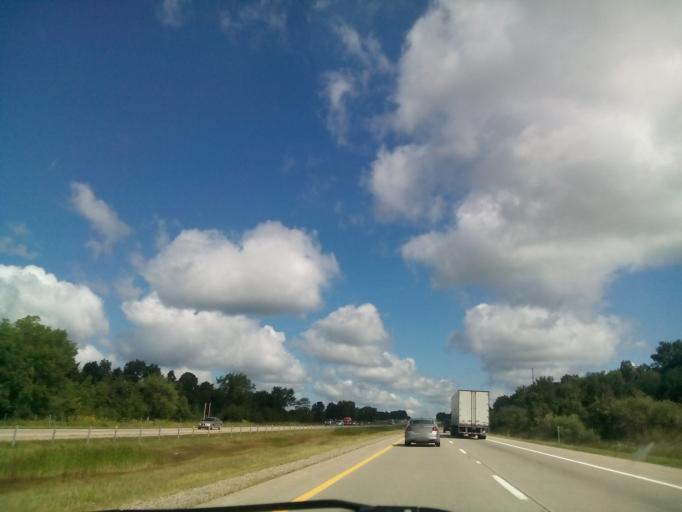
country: US
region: Michigan
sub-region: Genesee County
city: Linden
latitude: 42.7267
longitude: -83.7631
